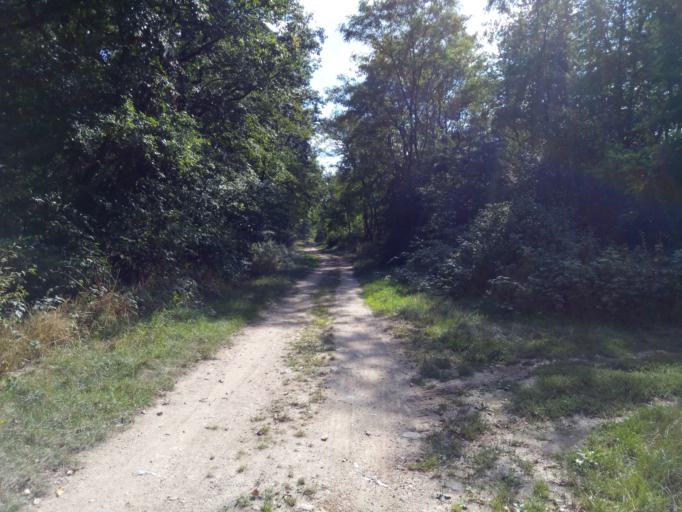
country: DE
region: Rheinland-Pfalz
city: Roth
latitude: 49.9307
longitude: 7.8119
